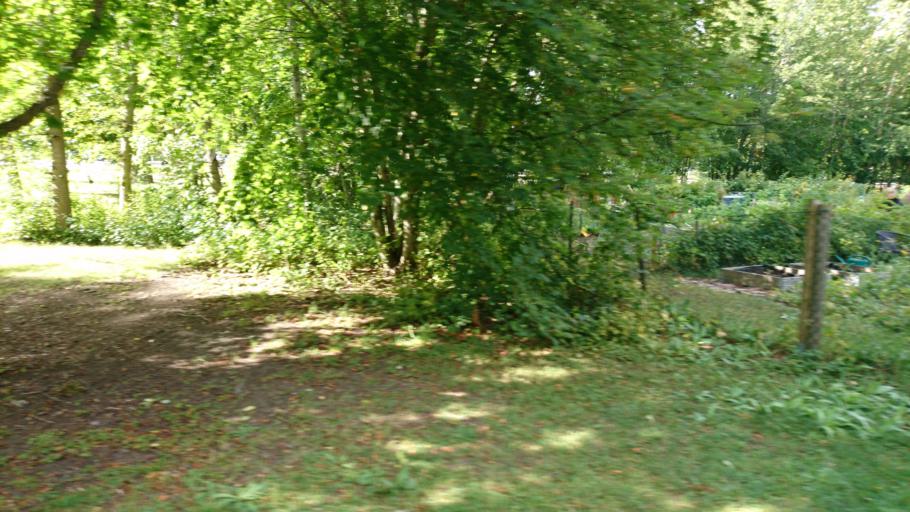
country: SE
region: Uppsala
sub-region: Uppsala Kommun
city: Uppsala
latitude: 59.8660
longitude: 17.6420
